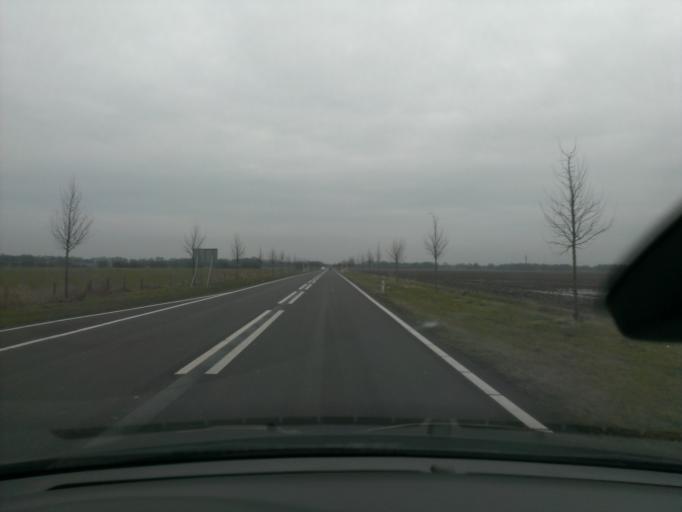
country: NL
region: Overijssel
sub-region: Gemeente Twenterand
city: Vriezenveen
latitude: 52.4036
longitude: 6.6449
